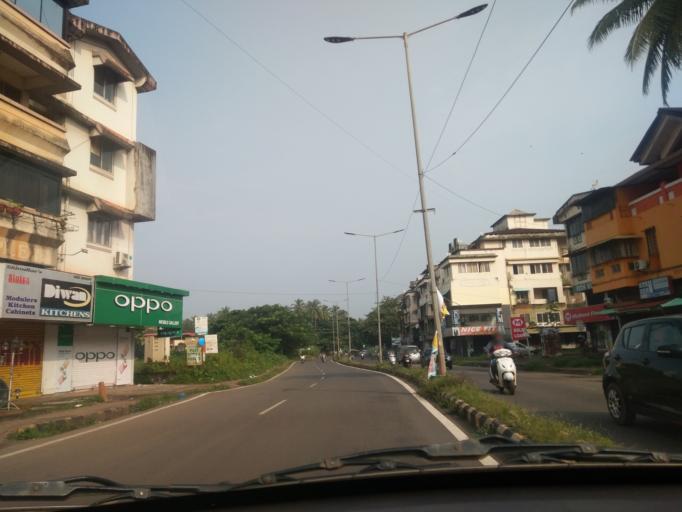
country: IN
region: Goa
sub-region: South Goa
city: Madgaon
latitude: 15.2619
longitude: 73.9631
